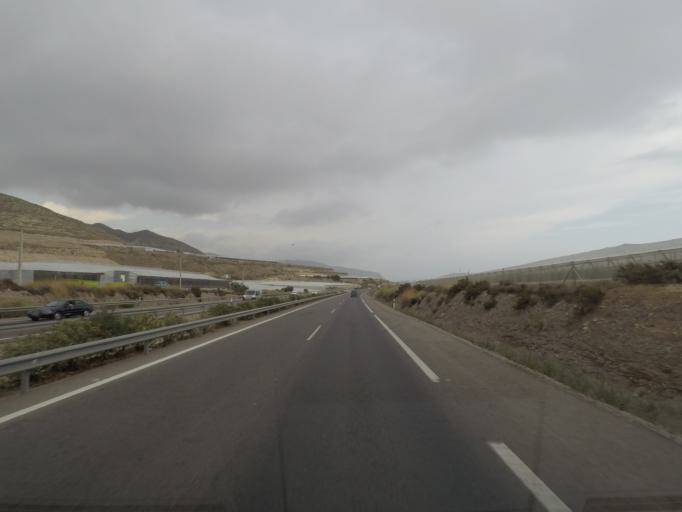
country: ES
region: Andalusia
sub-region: Provincia de Almeria
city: Vicar
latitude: 36.8120
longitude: -2.6261
